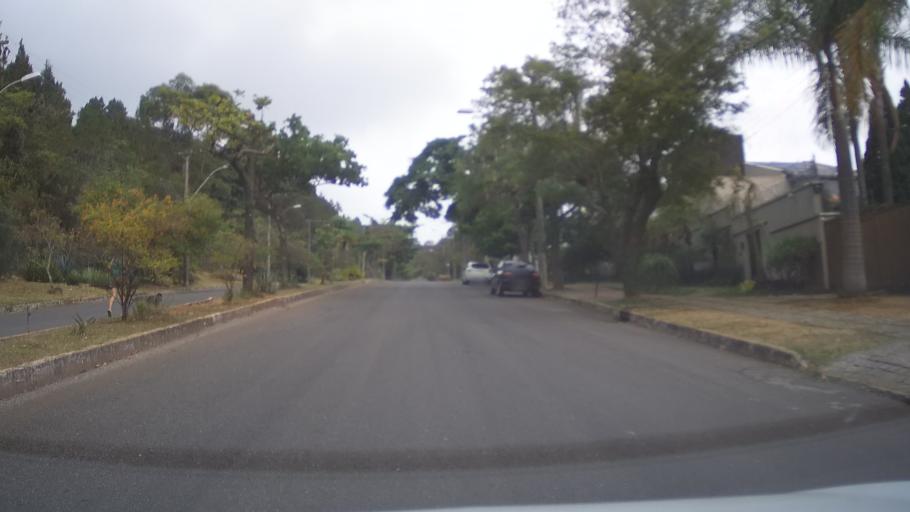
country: BR
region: Minas Gerais
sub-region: Belo Horizonte
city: Belo Horizonte
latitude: -19.9596
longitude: -43.9151
